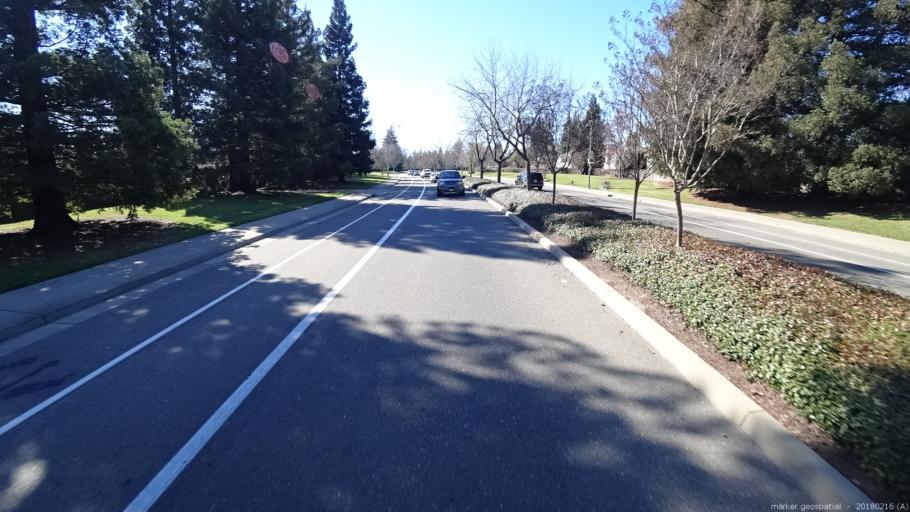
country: US
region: California
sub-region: Sacramento County
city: Gold River
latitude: 38.6279
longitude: -121.2293
